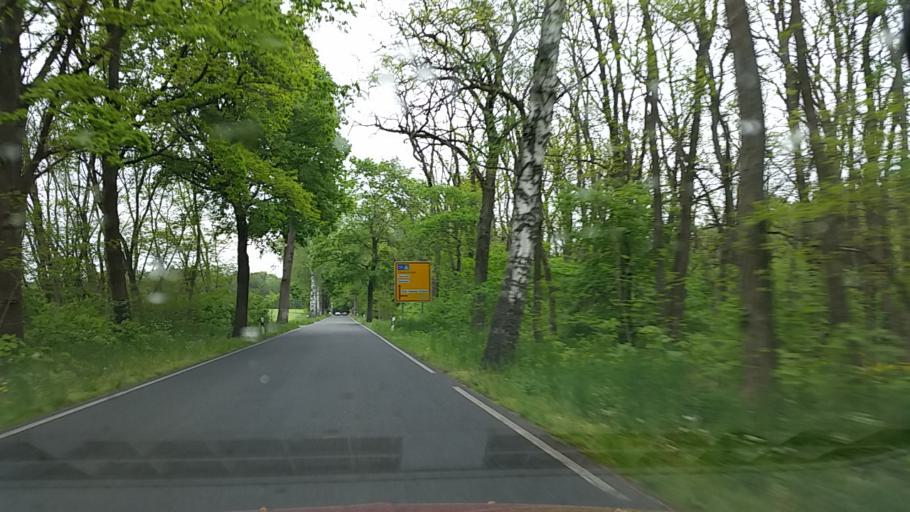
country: DE
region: Brandenburg
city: Diensdorf-Radlow
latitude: 52.2536
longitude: 14.0386
